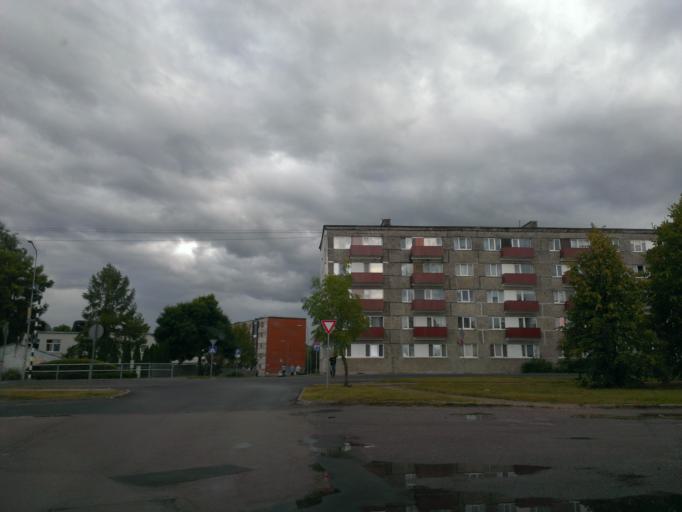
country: LV
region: Salaspils
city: Salaspils
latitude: 56.8532
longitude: 24.3388
